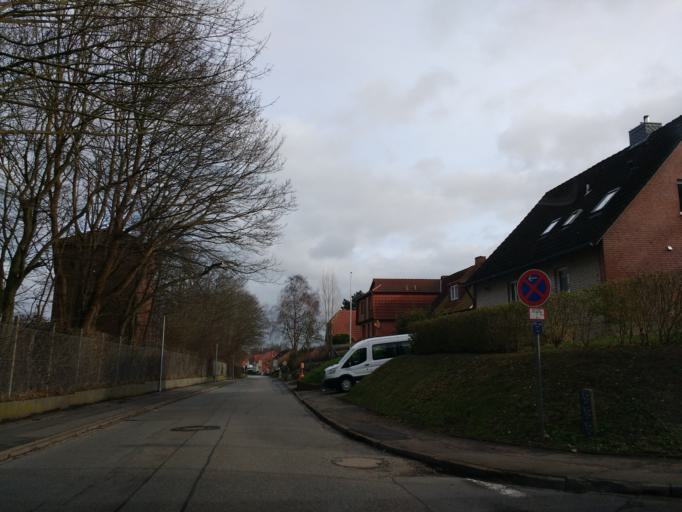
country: DE
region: Schleswig-Holstein
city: Heiligenhafen
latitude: 54.3719
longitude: 10.9606
